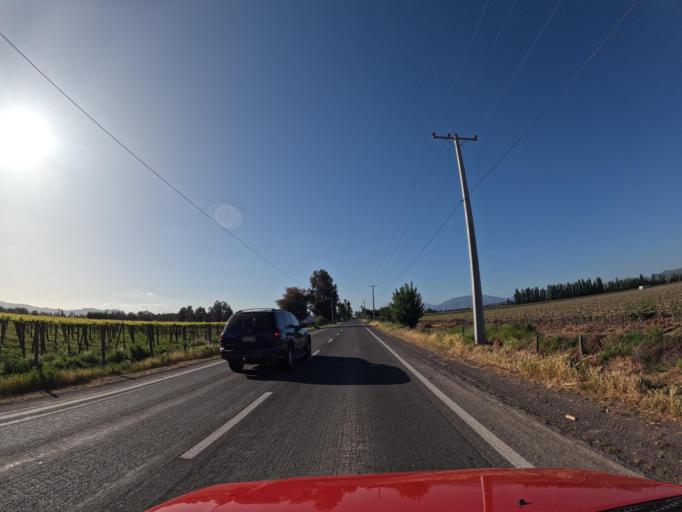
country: CL
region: Maule
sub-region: Provincia de Curico
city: Teno
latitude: -34.7638
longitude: -71.2376
